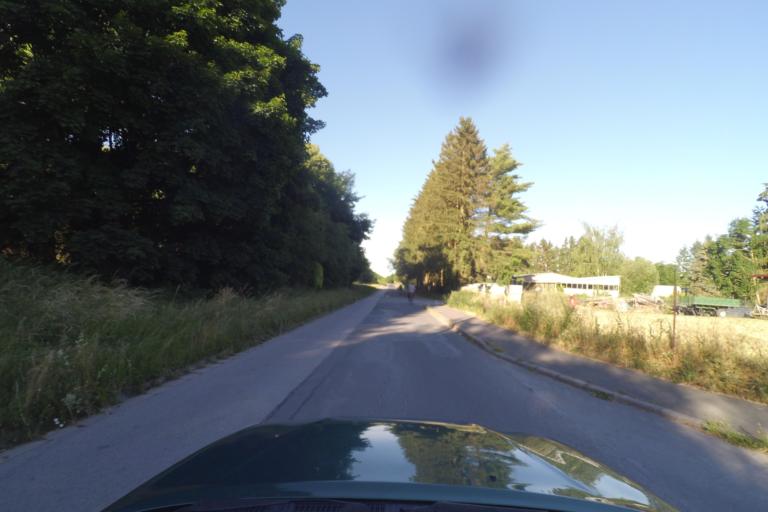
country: DE
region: Bavaria
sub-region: Upper Franconia
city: Speichersdorf
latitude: 49.8680
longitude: 11.7783
